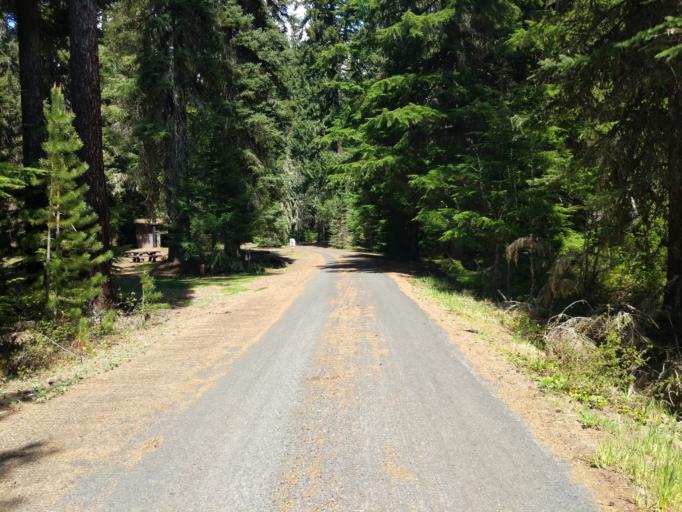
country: US
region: Oregon
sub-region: Clackamas County
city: Mount Hood Village
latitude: 45.1479
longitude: -121.7462
